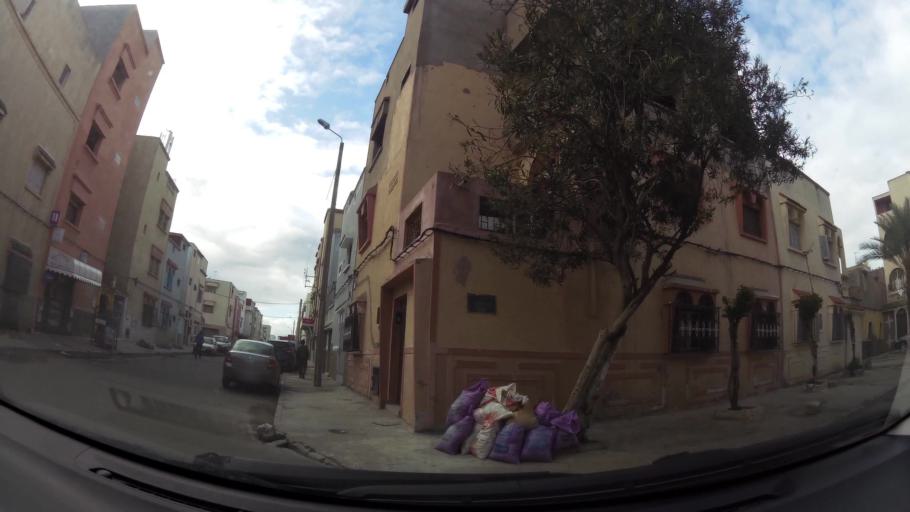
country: MA
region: Doukkala-Abda
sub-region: El-Jadida
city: El Jadida
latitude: 33.2423
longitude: -8.5312
